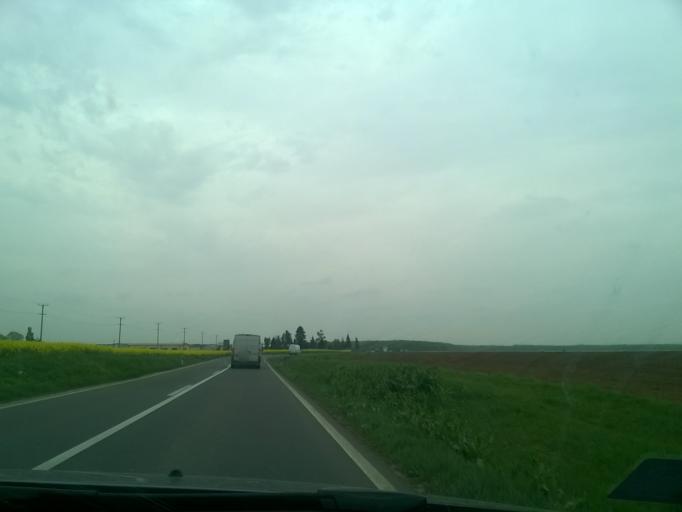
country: RS
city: Hrtkovci
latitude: 44.8523
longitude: 19.7708
